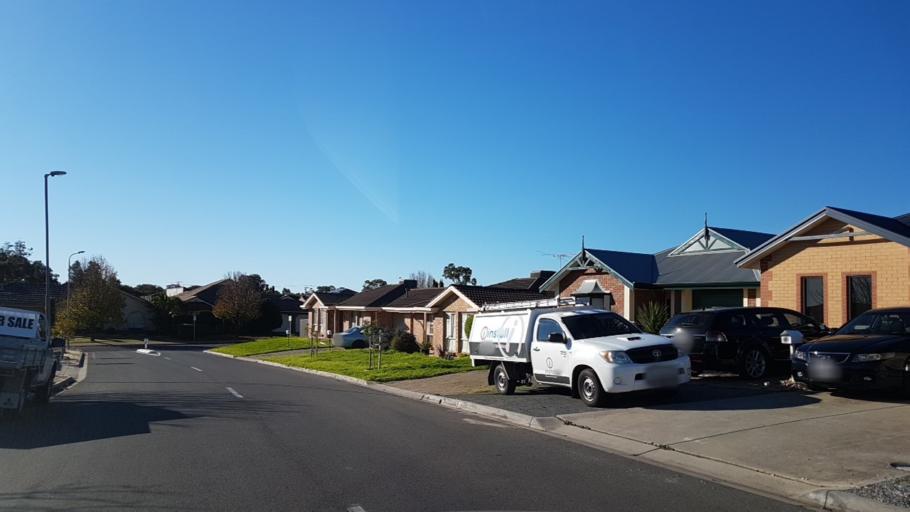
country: AU
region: South Australia
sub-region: Campbelltown
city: Athelstone
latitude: -34.8833
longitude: 138.6861
